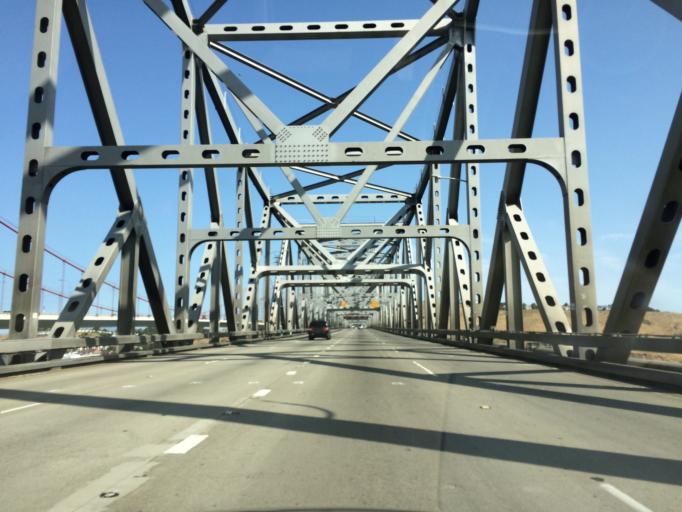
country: US
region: California
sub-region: Contra Costa County
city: Crockett
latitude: 38.0579
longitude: -122.2249
